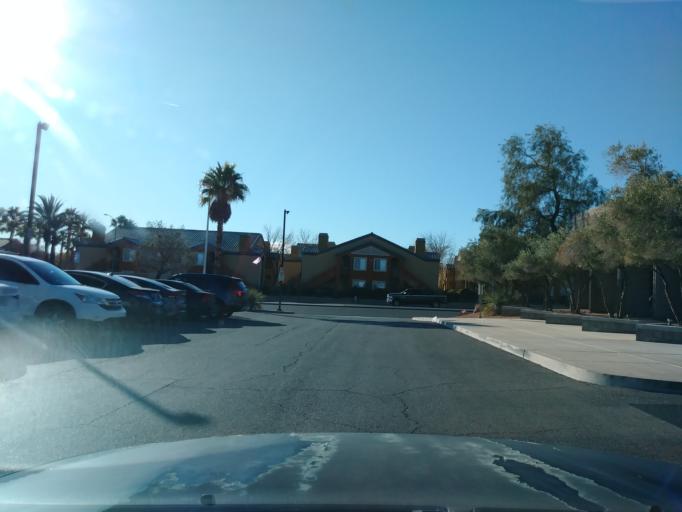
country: US
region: Nevada
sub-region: Clark County
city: Spring Valley
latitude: 36.1596
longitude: -115.2490
